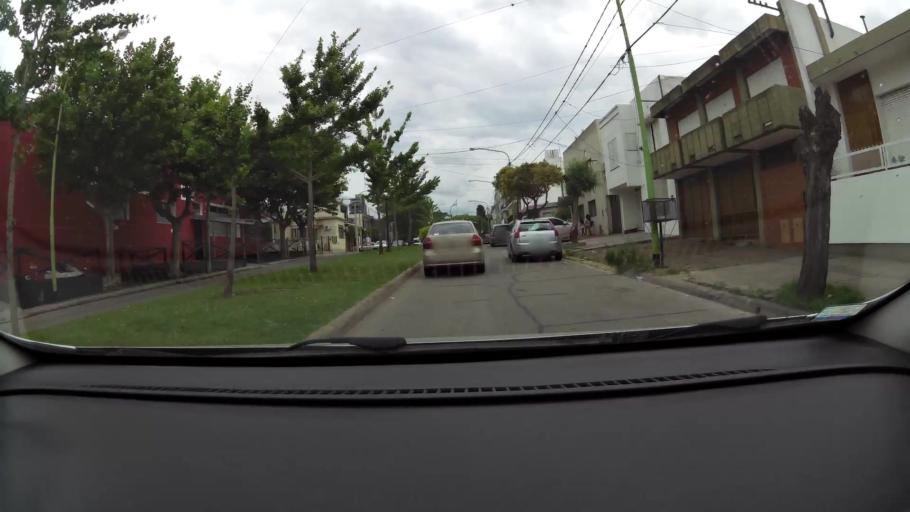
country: AR
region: Buenos Aires
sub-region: Partido de Campana
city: Campana
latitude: -34.1634
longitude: -58.9564
